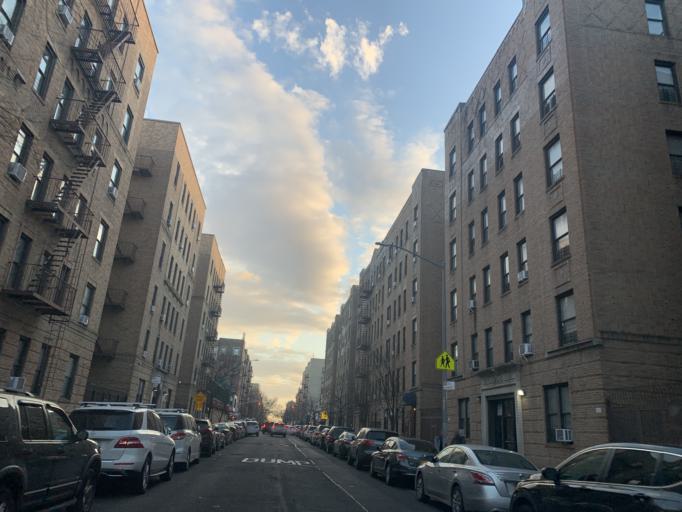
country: US
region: New York
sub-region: Bronx
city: The Bronx
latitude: 40.8556
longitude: -73.8657
